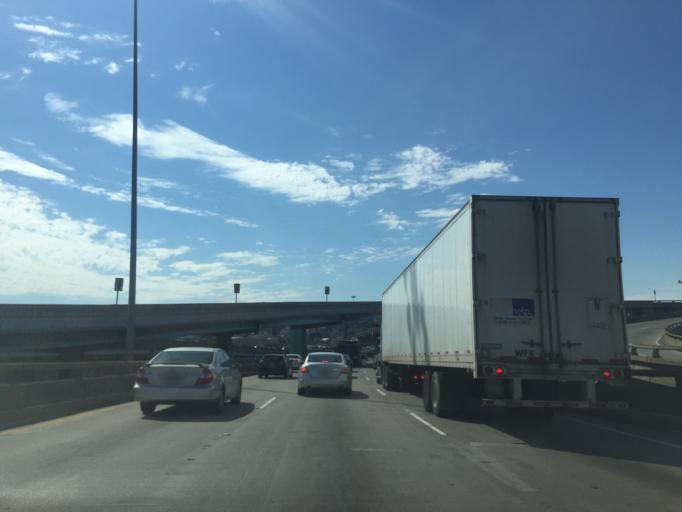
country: US
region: California
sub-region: San Francisco County
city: San Francisco
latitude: 37.7702
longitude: -122.4058
